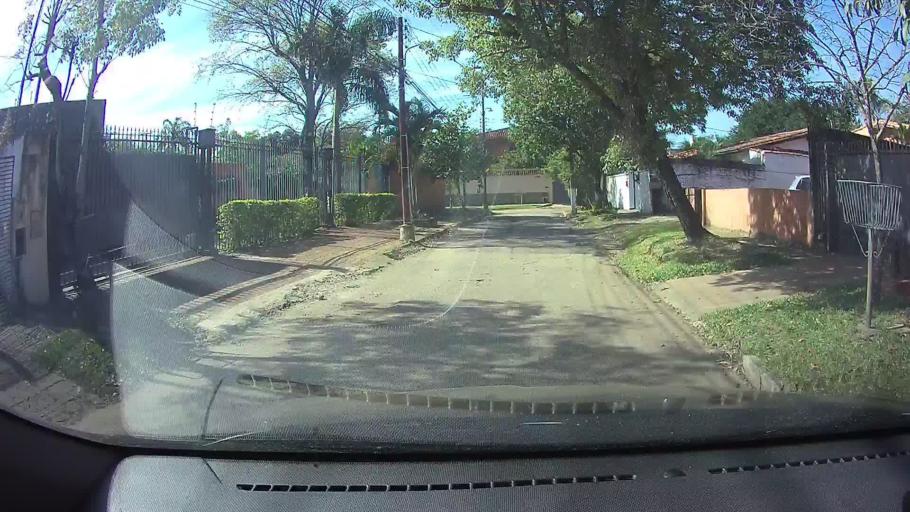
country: PY
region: Central
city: Fernando de la Mora
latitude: -25.2832
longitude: -57.5432
